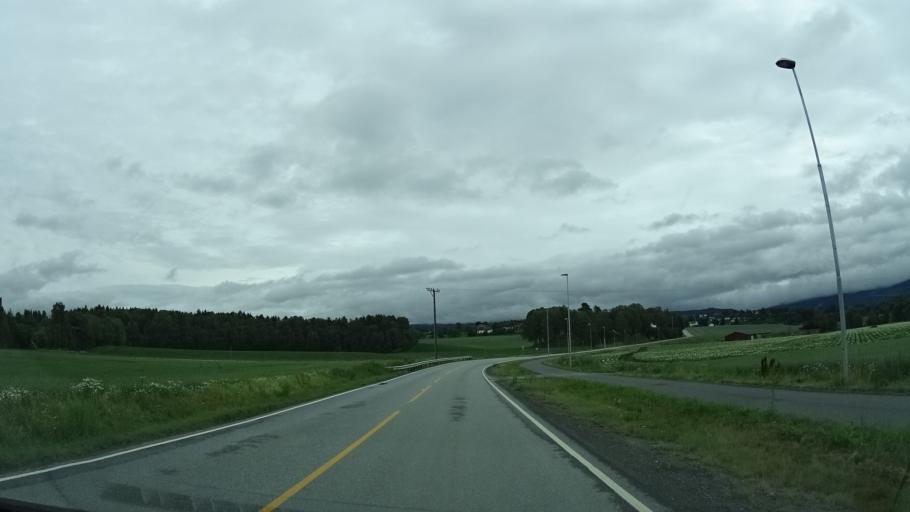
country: NO
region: Buskerud
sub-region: Ringerike
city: Honefoss
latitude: 60.1289
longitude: 10.2522
